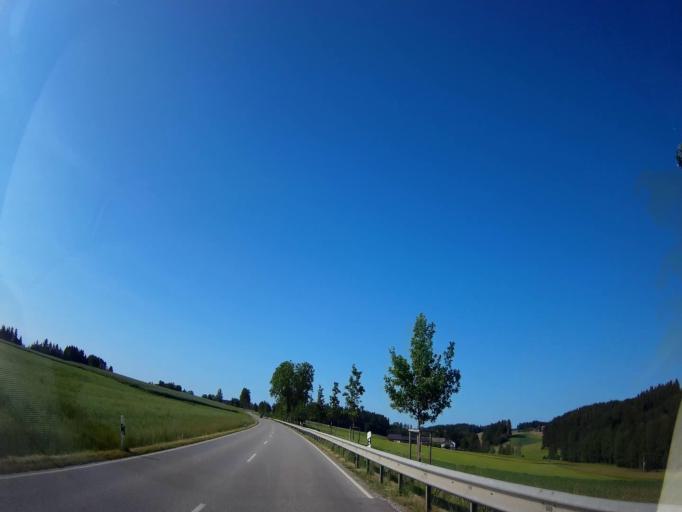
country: DE
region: Bavaria
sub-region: Lower Bavaria
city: Zeilarn
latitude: 48.3151
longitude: 12.8295
